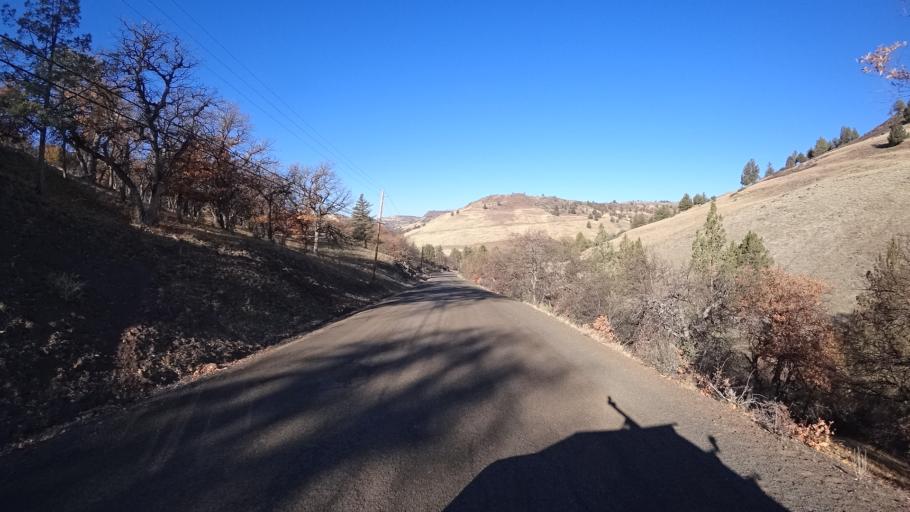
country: US
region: California
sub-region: Siskiyou County
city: Montague
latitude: 41.9157
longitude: -122.4447
